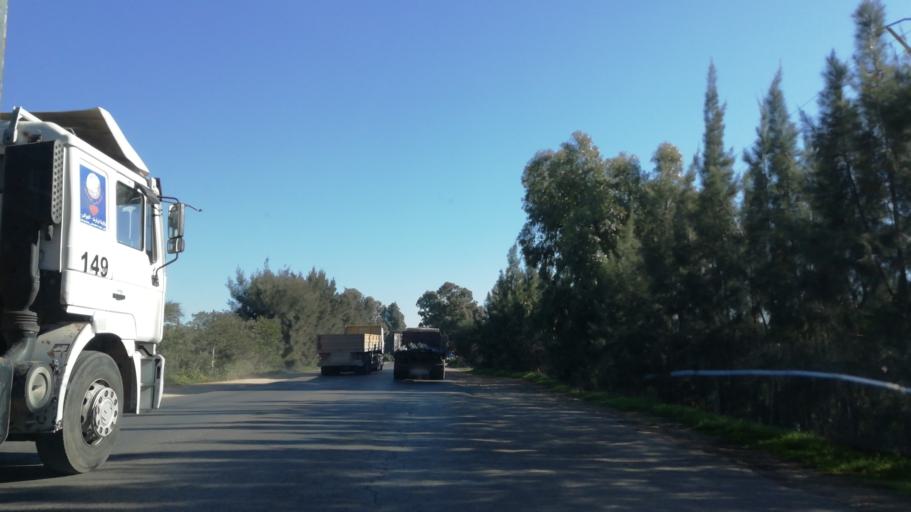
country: DZ
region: Relizane
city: Zemoura
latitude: 35.7441
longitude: 0.7007
